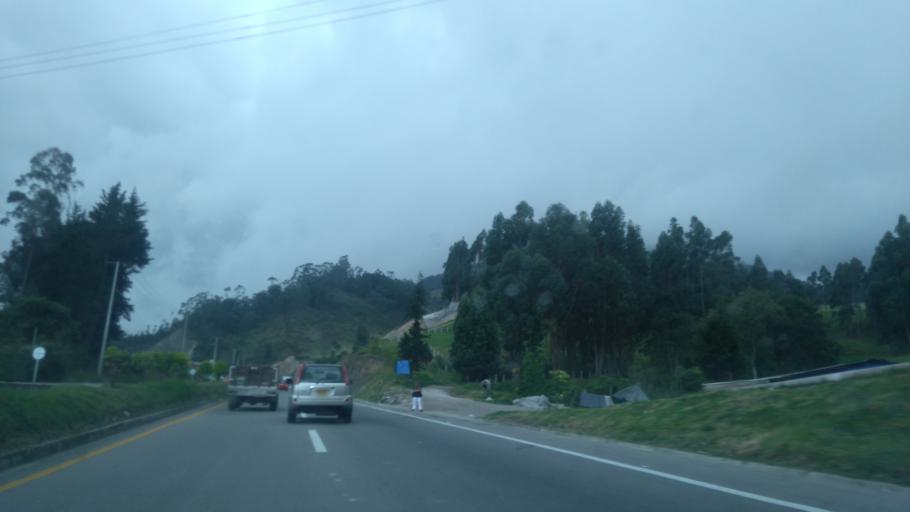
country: CO
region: Cundinamarca
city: El Rosal
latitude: 4.8949
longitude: -74.3069
